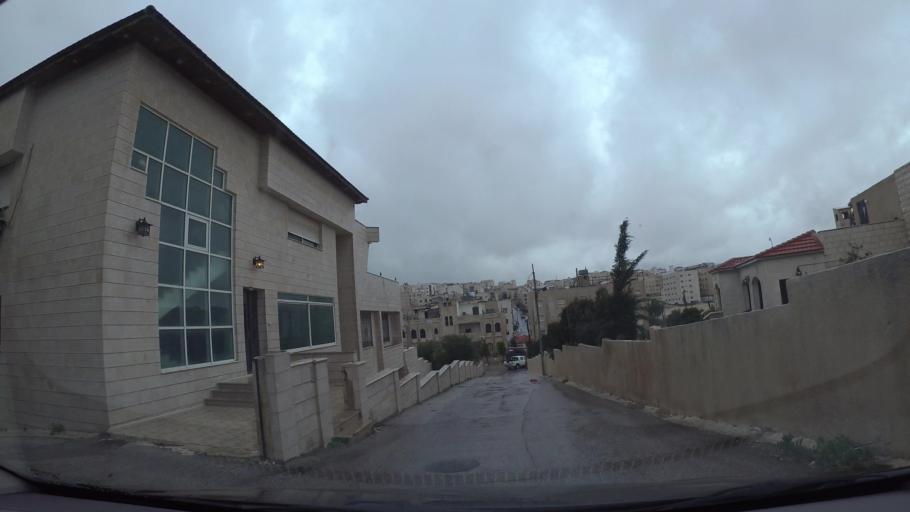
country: JO
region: Amman
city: Al Jubayhah
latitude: 32.0235
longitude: 35.8734
